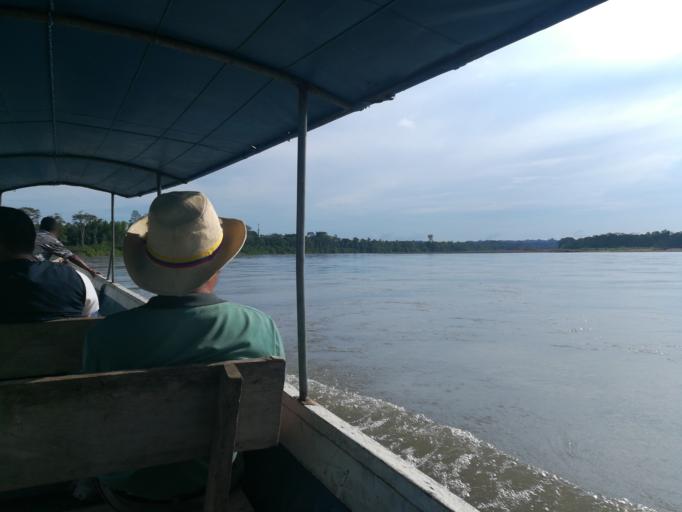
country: EC
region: Orellana
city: Boca Suno
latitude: -0.8361
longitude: -77.1942
